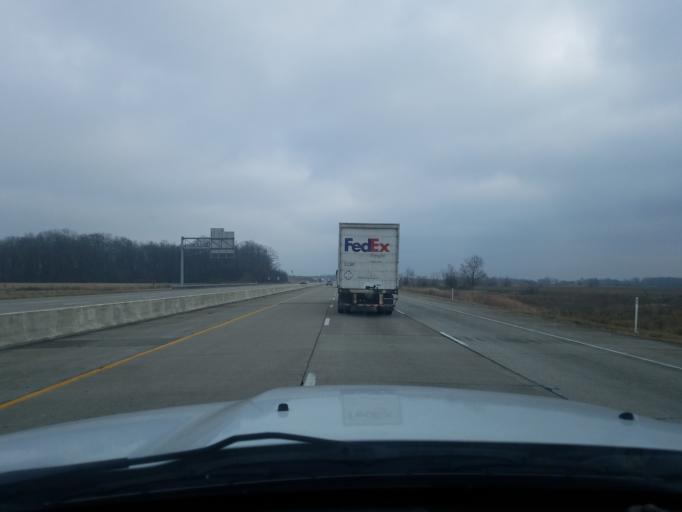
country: US
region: Indiana
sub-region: Huntington County
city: Roanoke
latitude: 40.9566
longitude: -85.2657
